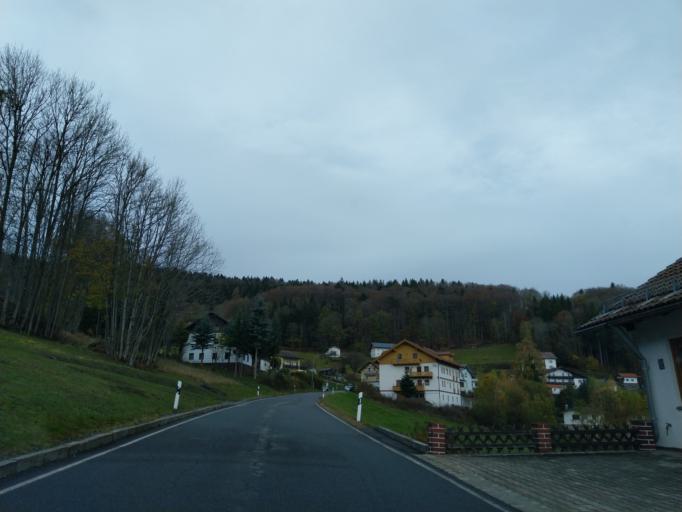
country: DE
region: Bavaria
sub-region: Lower Bavaria
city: Schofweg
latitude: 48.8126
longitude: 13.2314
